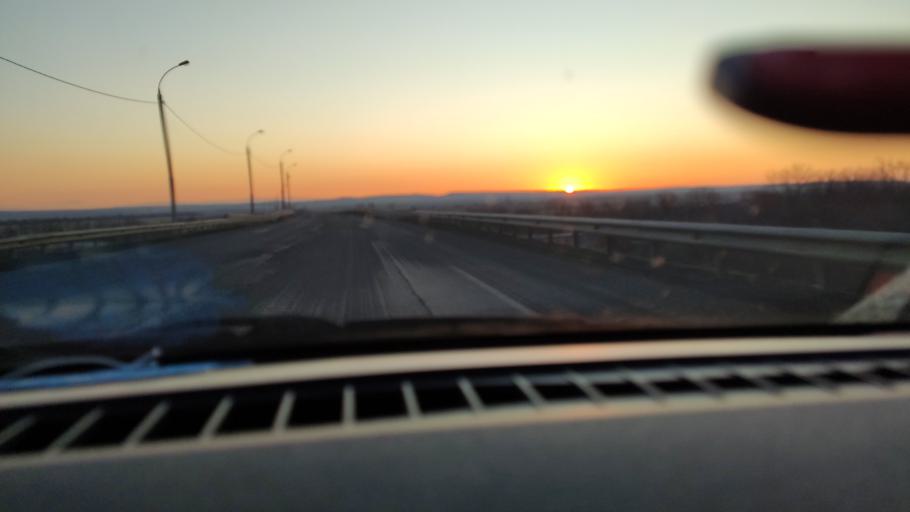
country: RU
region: Saratov
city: Yelshanka
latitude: 51.8000
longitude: 46.1858
